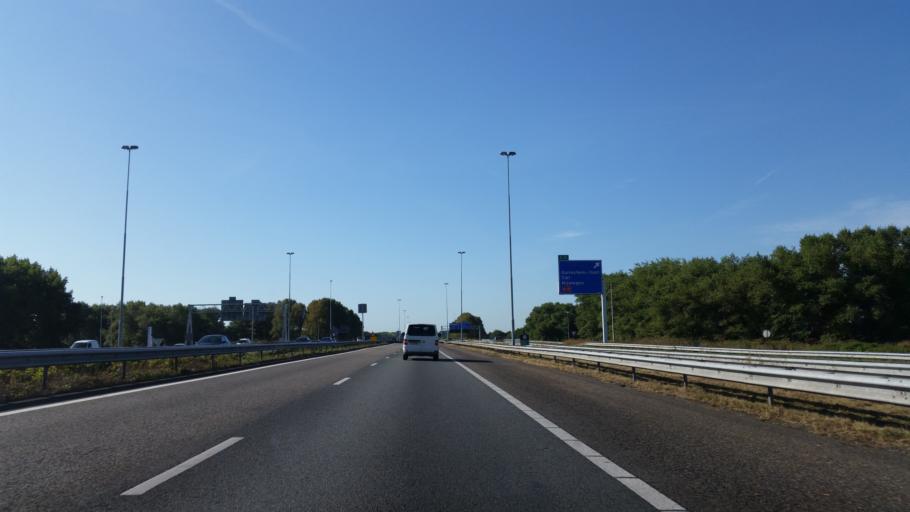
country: NL
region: South Holland
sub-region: Gemeente Gorinchem
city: Gorinchem
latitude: 51.8482
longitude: 4.9514
